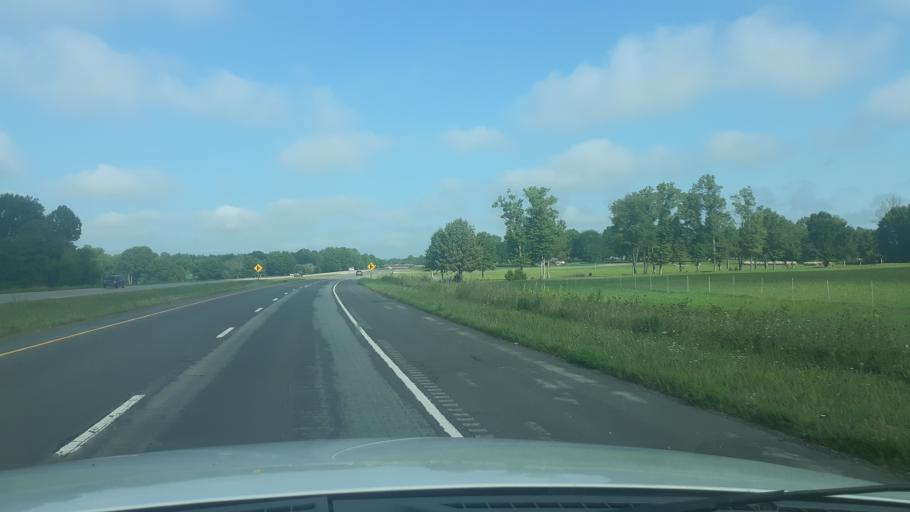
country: US
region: Illinois
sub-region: Saline County
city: Carrier Mills
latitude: 37.7352
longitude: -88.7010
